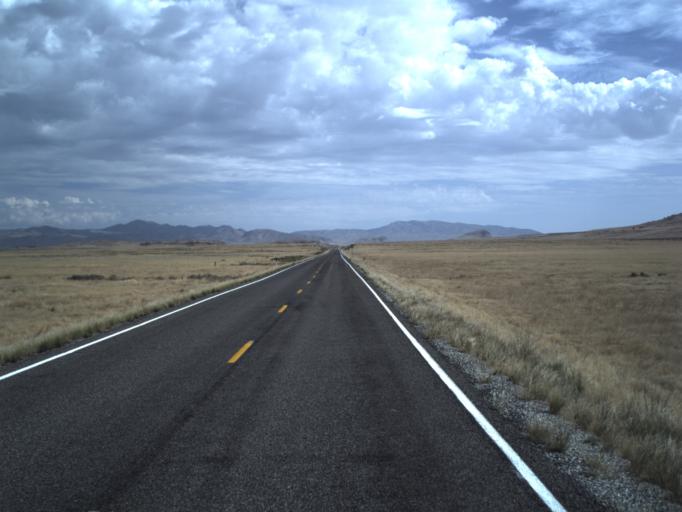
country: US
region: Utah
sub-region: Tooele County
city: Wendover
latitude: 41.3997
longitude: -113.9529
